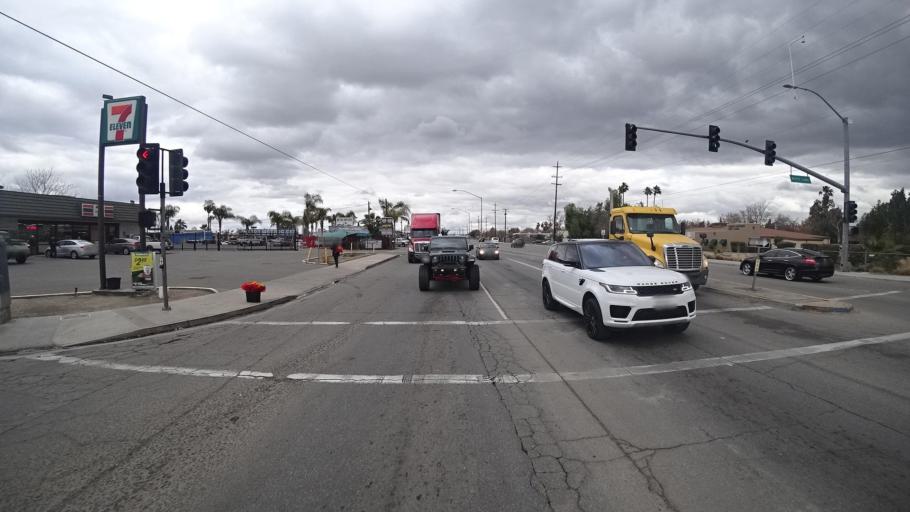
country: US
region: California
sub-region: Kern County
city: Greenfield
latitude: 35.3178
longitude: -119.0031
